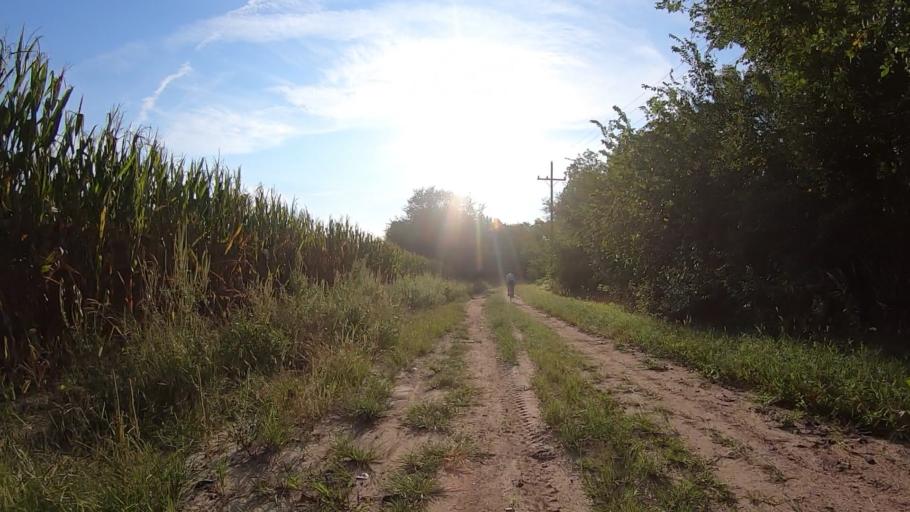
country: US
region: Kansas
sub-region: Marshall County
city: Blue Rapids
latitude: 39.7119
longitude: -96.7805
